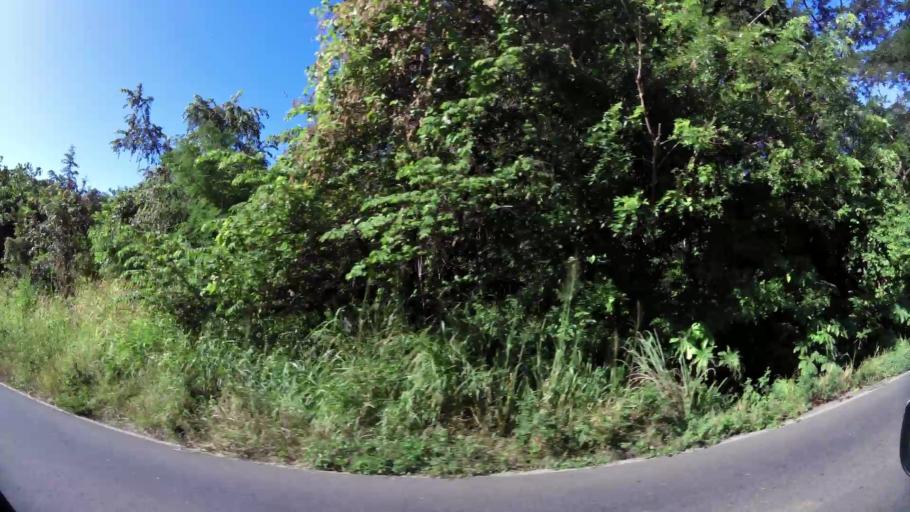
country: CR
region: Guanacaste
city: Belen
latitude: 10.3630
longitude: -85.7513
